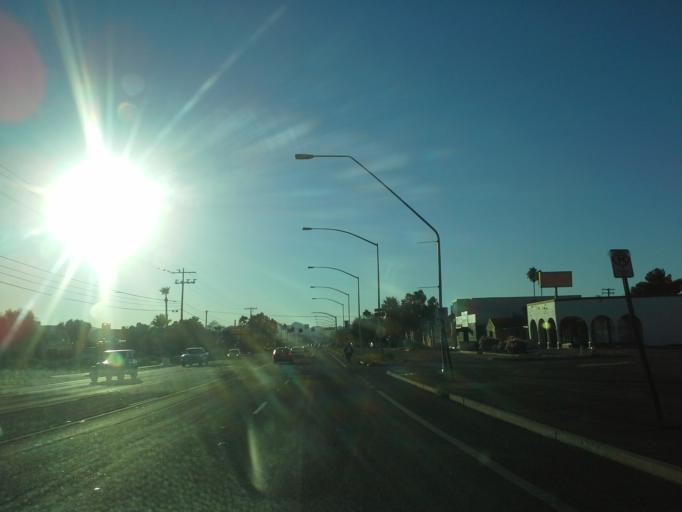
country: US
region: Arizona
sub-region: Pima County
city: Tucson
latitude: 32.2216
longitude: -110.9287
